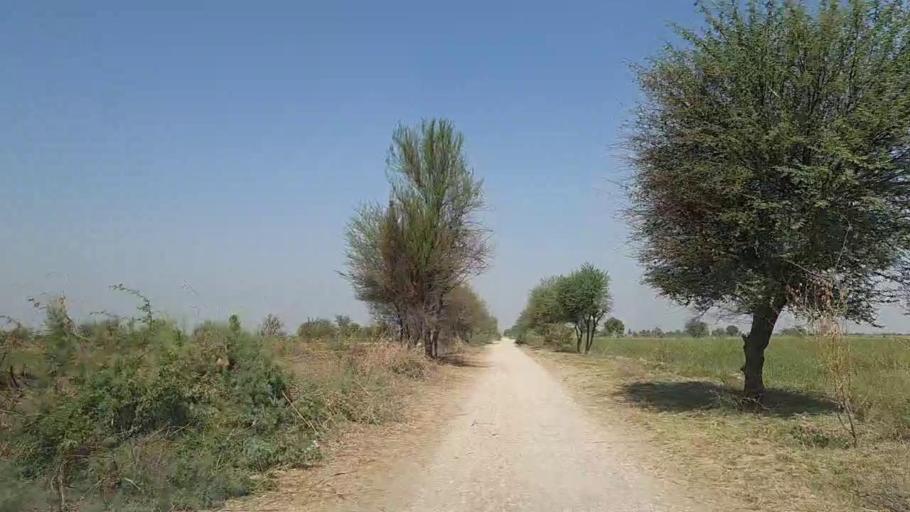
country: PK
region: Sindh
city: Samaro
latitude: 25.1948
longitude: 69.4041
